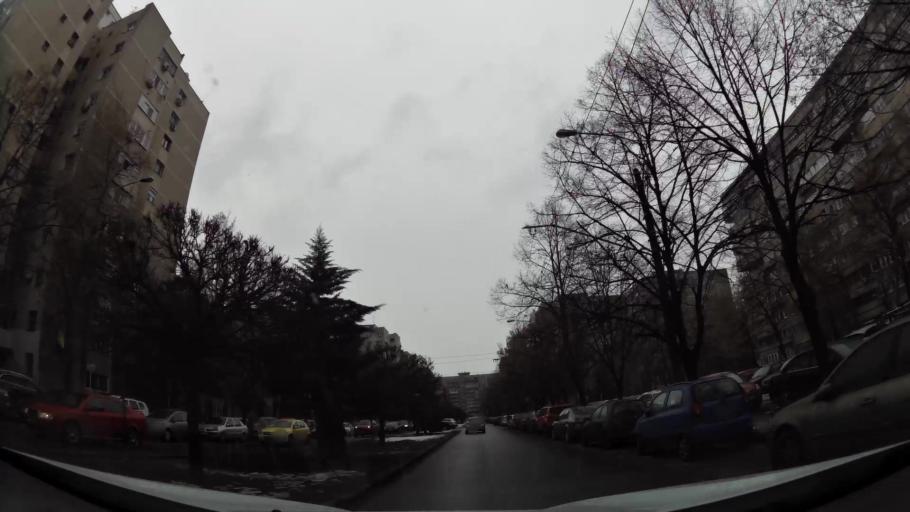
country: RO
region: Ilfov
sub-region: Comuna Chiajna
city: Rosu
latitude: 44.4223
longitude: 26.0474
